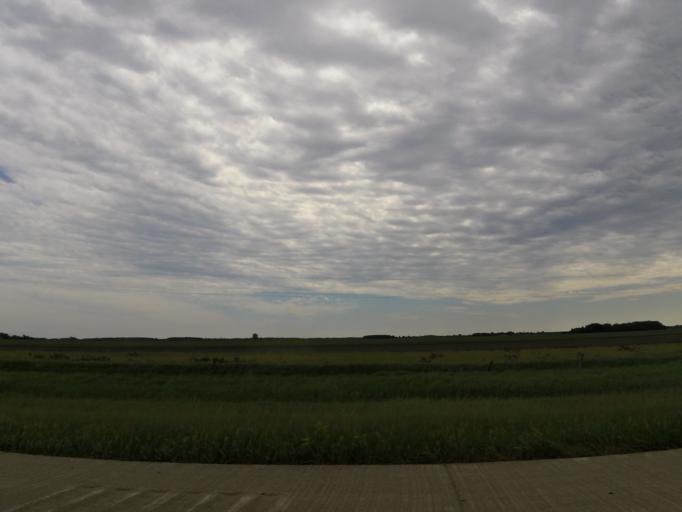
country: US
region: North Dakota
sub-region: Walsh County
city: Grafton
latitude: 48.3724
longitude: -97.1900
